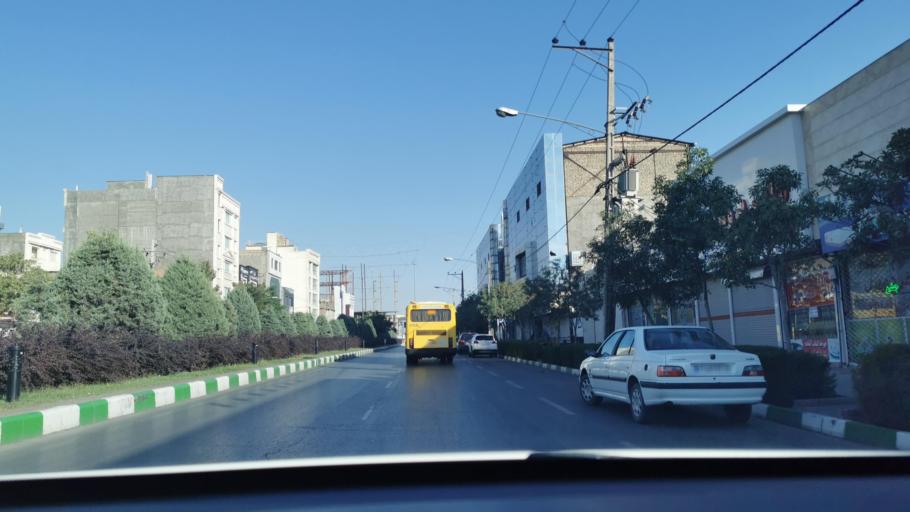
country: IR
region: Razavi Khorasan
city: Mashhad
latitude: 36.3059
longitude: 59.5107
